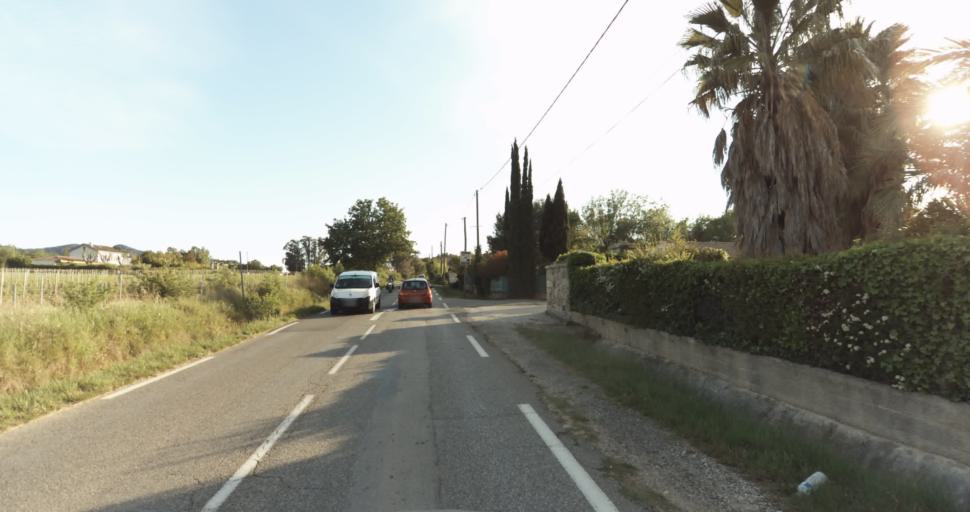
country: FR
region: Provence-Alpes-Cote d'Azur
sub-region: Departement du Var
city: La Crau
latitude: 43.1659
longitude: 6.1054
